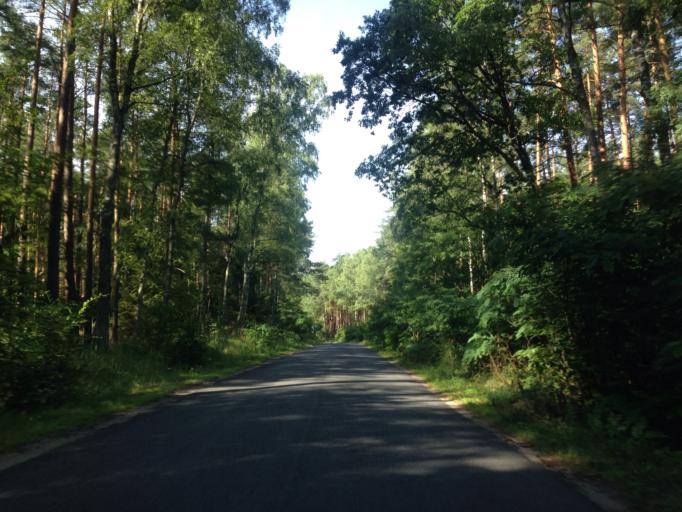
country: PL
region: Pomeranian Voivodeship
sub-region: Powiat starogardzki
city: Osiek
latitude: 53.7622
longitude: 18.4654
